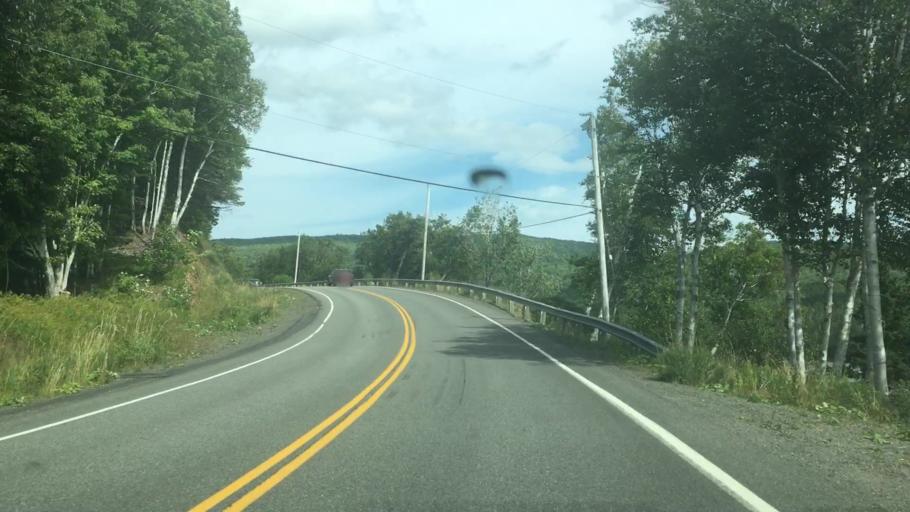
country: CA
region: Nova Scotia
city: Sydney Mines
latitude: 46.2664
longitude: -60.6090
